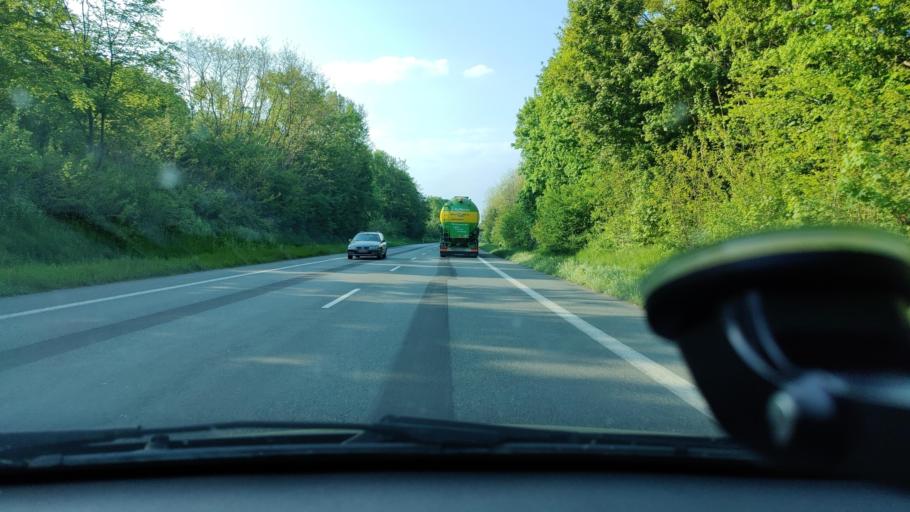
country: DE
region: North Rhine-Westphalia
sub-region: Regierungsbezirk Munster
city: Telgte
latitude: 51.9844
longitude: 7.8107
